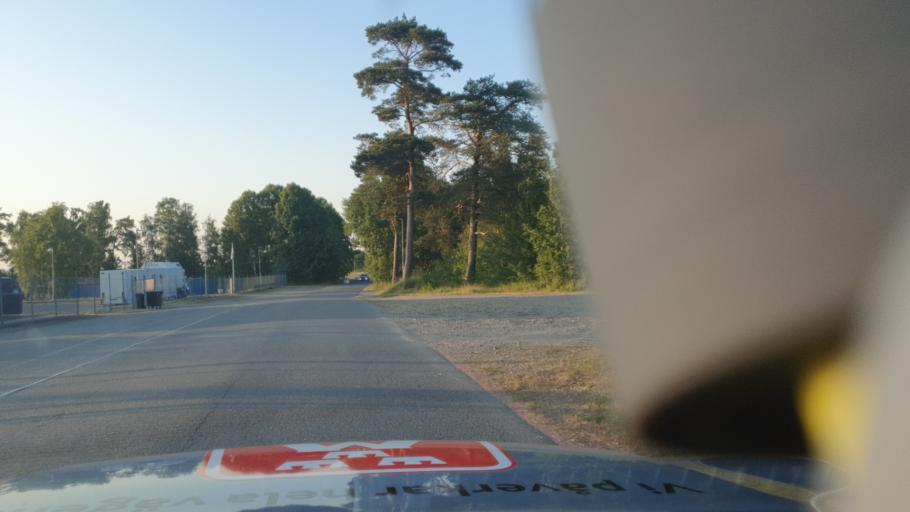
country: SE
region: Skane
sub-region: Kristianstads Kommun
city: Norra Asum
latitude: 55.9879
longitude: 14.1352
